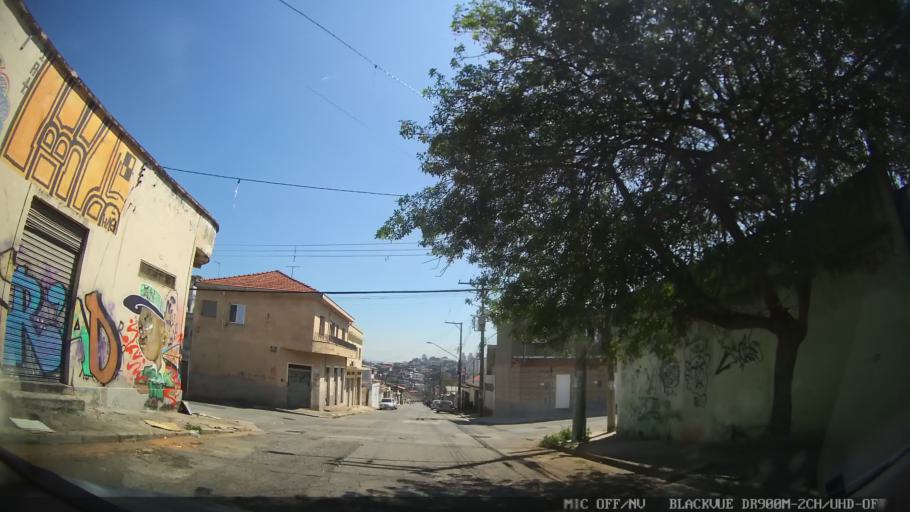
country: BR
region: Sao Paulo
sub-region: Sao Paulo
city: Sao Paulo
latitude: -23.4951
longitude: -46.6548
